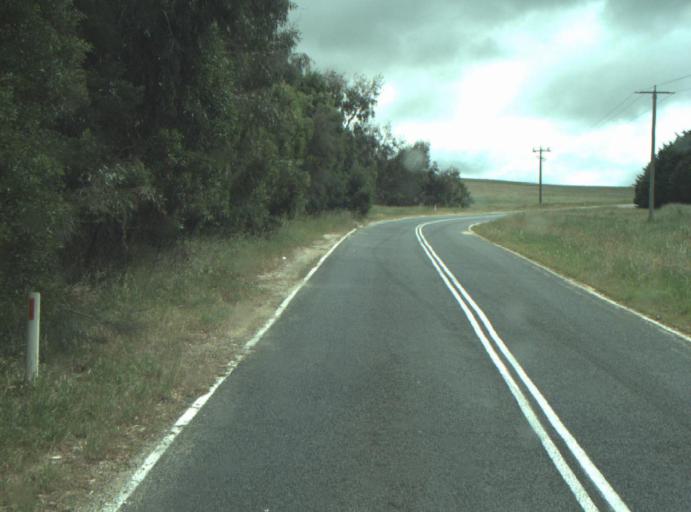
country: AU
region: Victoria
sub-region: Greater Geelong
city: Wandana Heights
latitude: -38.1951
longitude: 144.2641
